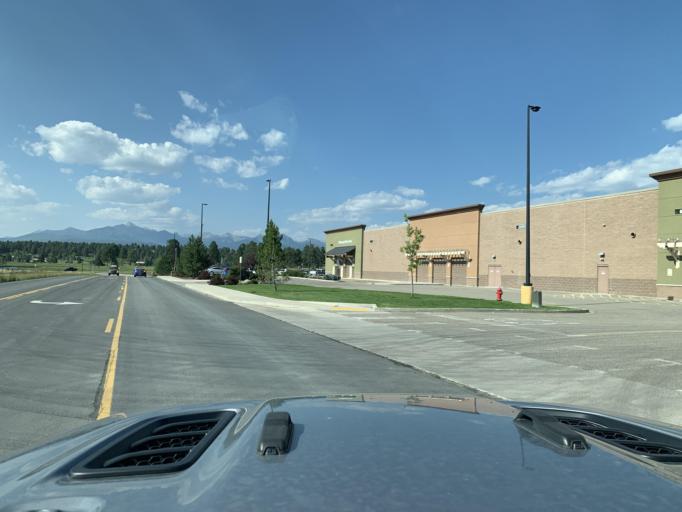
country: US
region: Colorado
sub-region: Archuleta County
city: Pagosa Springs
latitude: 37.2591
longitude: -107.0643
